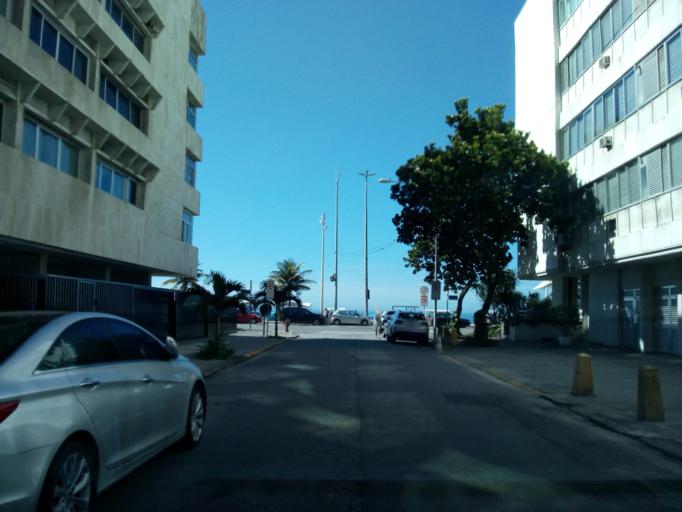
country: BR
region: Rio de Janeiro
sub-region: Rio De Janeiro
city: Rio de Janeiro
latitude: -22.9858
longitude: -43.2186
